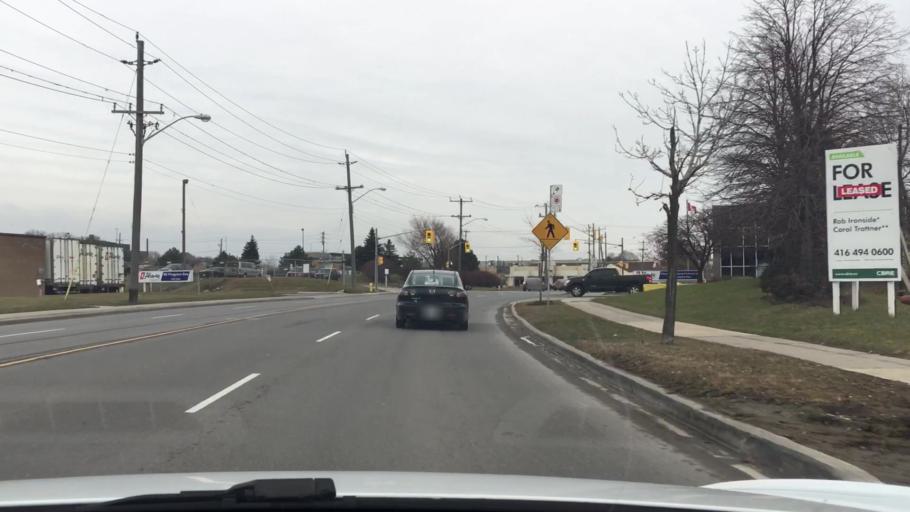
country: CA
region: Ontario
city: Scarborough
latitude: 43.7721
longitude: -79.2757
